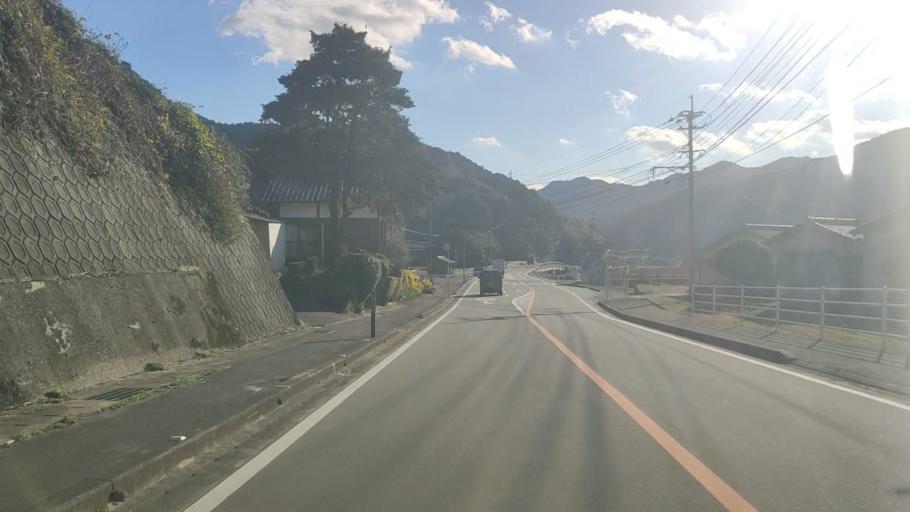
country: JP
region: Saga Prefecture
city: Saga-shi
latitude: 33.3610
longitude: 130.2537
